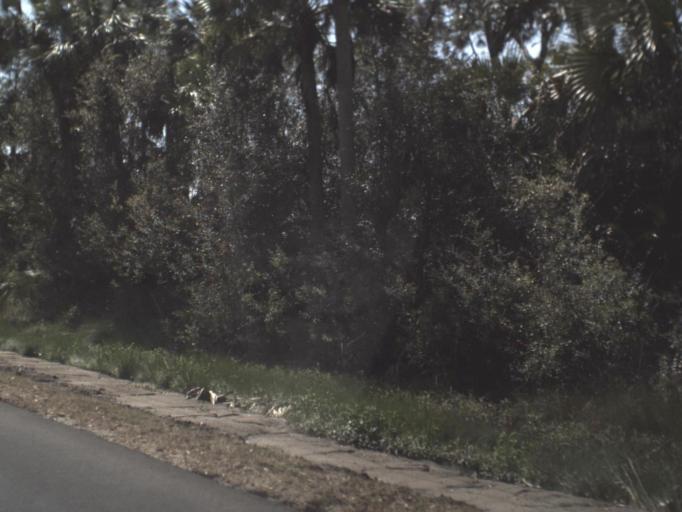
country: US
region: Florida
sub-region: Gulf County
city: Port Saint Joe
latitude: 29.7269
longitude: -85.3029
